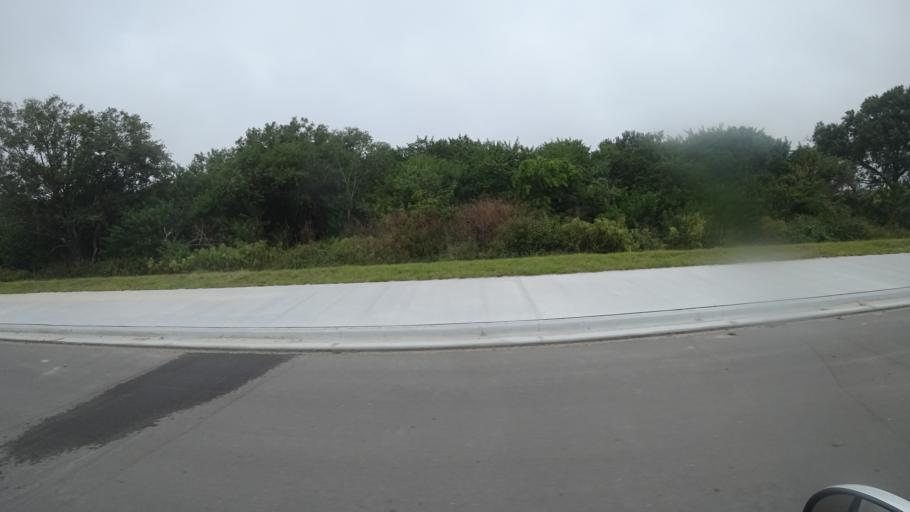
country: US
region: Florida
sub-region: Sarasota County
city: The Meadows
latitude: 27.4442
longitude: -82.3511
